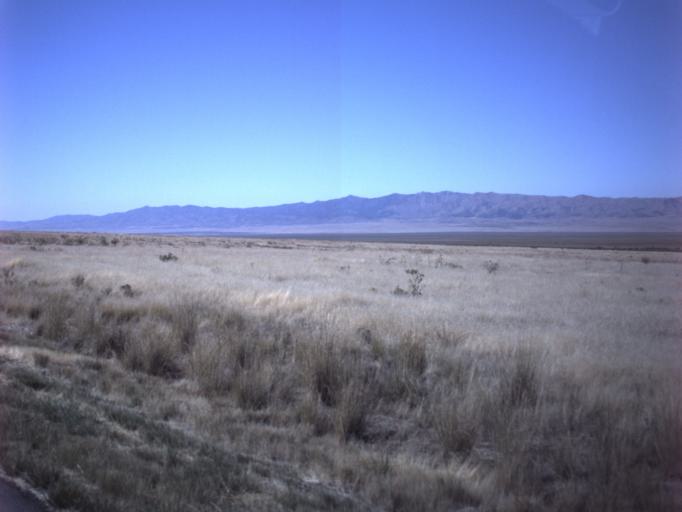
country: US
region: Utah
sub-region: Tooele County
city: Grantsville
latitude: 40.5995
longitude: -112.7142
